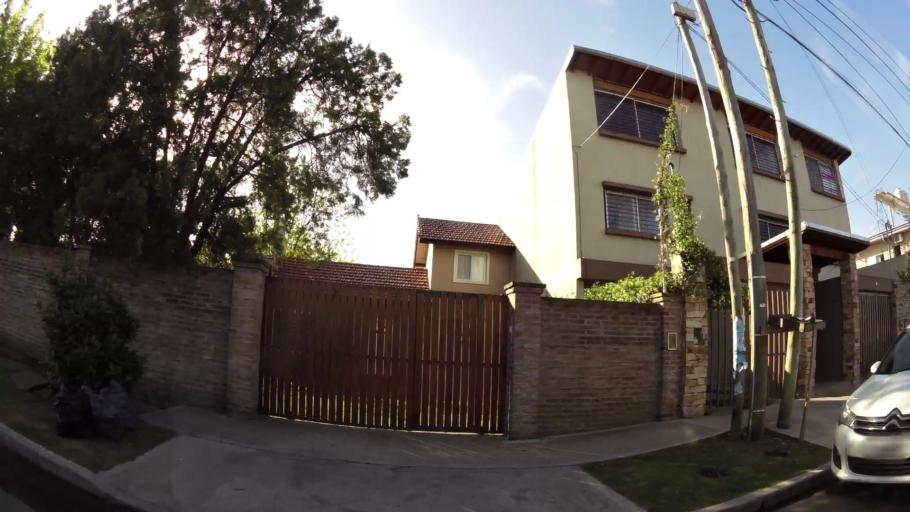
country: AR
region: Buenos Aires
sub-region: Partido de Quilmes
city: Quilmes
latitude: -34.8100
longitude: -58.2103
